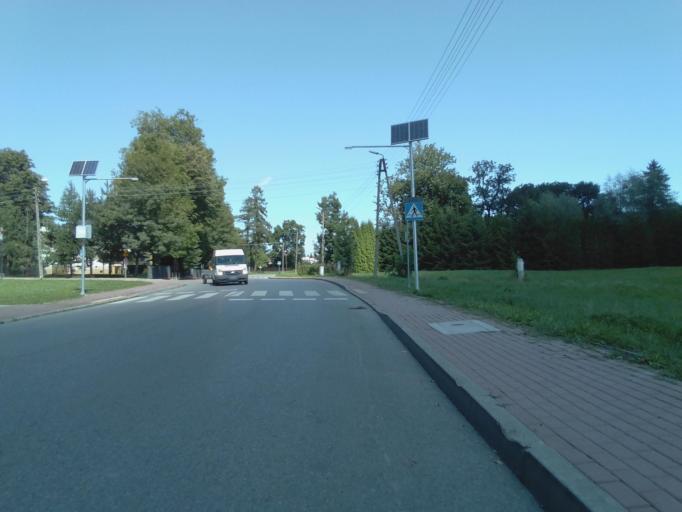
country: PL
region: Subcarpathian Voivodeship
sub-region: Powiat krosnienski
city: Jedlicze
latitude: 49.7141
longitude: 21.6380
